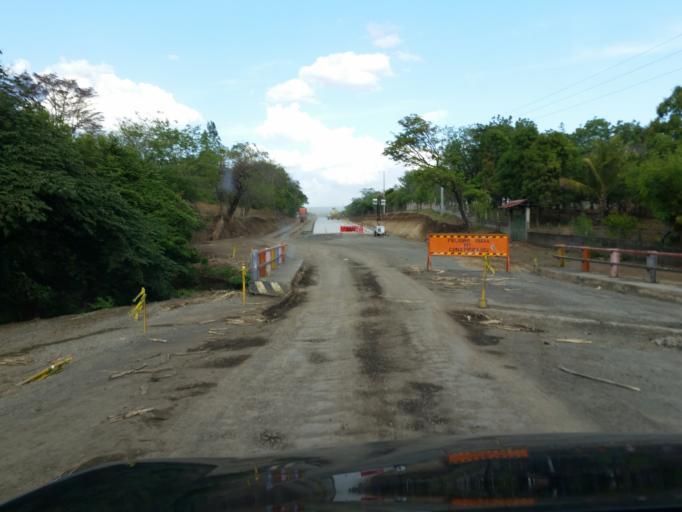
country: NI
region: Managua
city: Carlos Fonseca Amador
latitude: 12.0723
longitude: -86.4929
